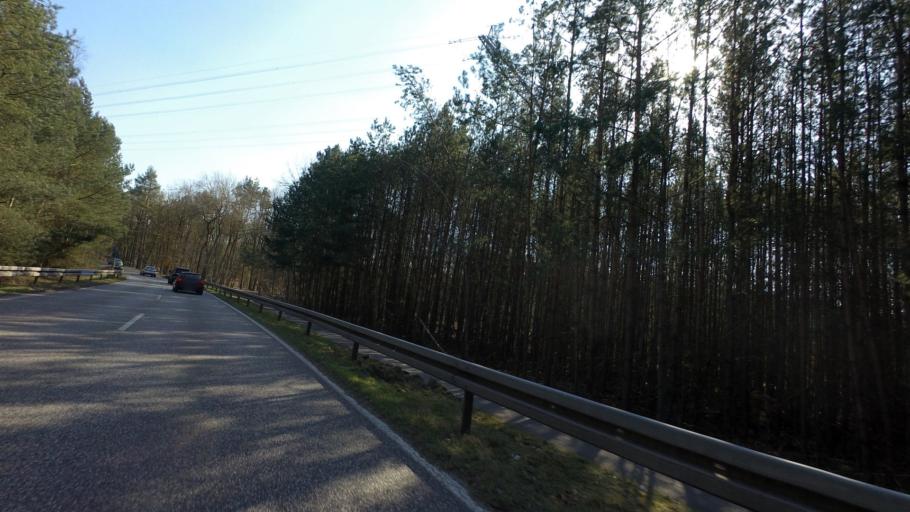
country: DE
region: Berlin
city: Konradshohe
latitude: 52.5887
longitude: 13.2021
